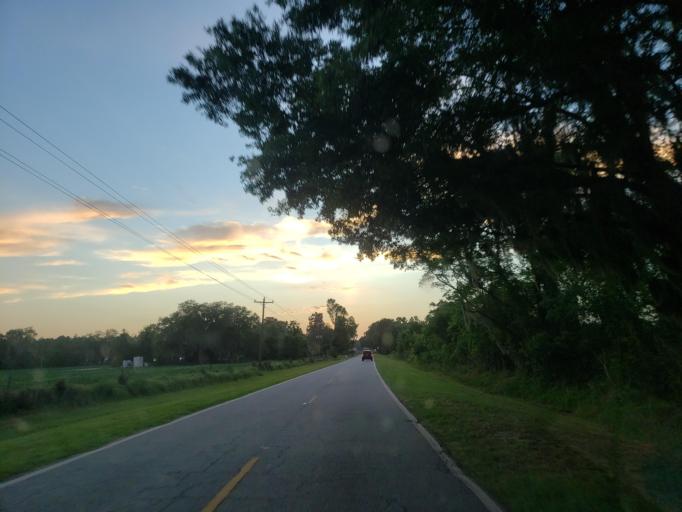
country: US
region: Georgia
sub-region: Echols County
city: Statenville
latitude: 30.6631
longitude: -83.2028
